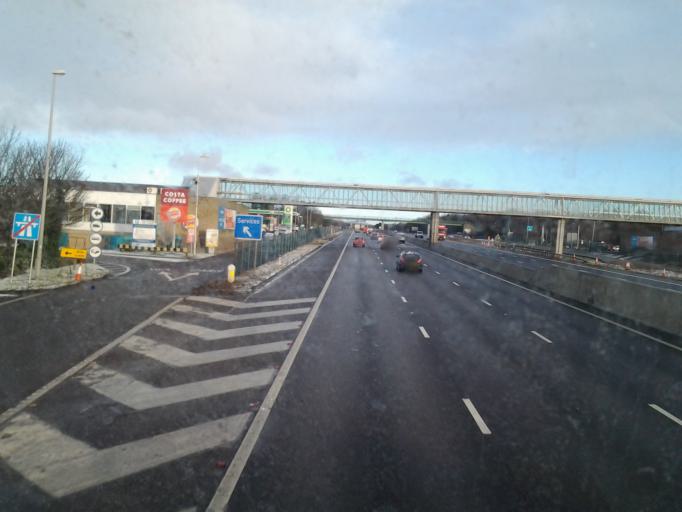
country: GB
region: England
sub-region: County Durham
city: Chester-le-Street
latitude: 54.8885
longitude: -1.5595
